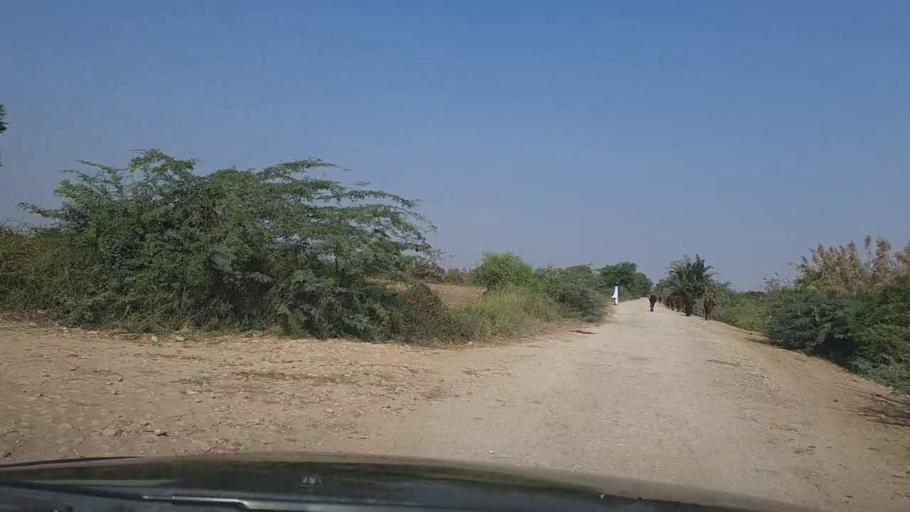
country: PK
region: Sindh
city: Thatta
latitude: 24.6302
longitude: 67.8136
